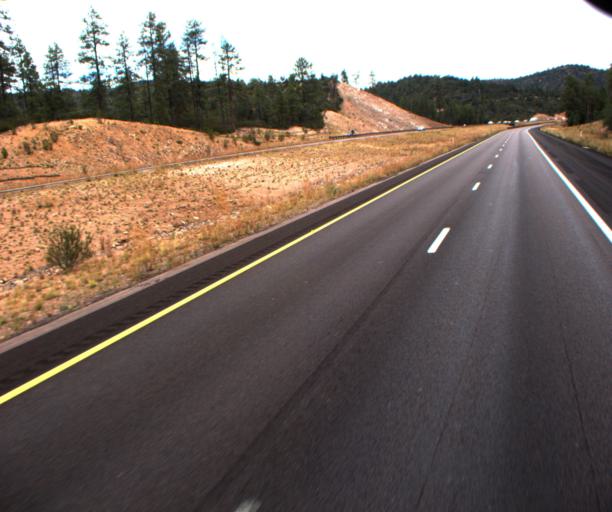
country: US
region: Arizona
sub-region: Gila County
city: Star Valley
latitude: 34.2868
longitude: -111.1408
